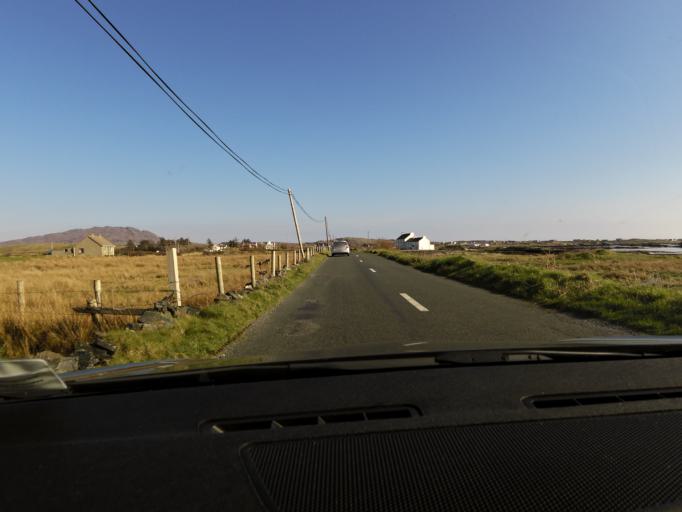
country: IE
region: Connaught
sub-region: County Galway
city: Clifden
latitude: 53.4114
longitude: -10.0399
